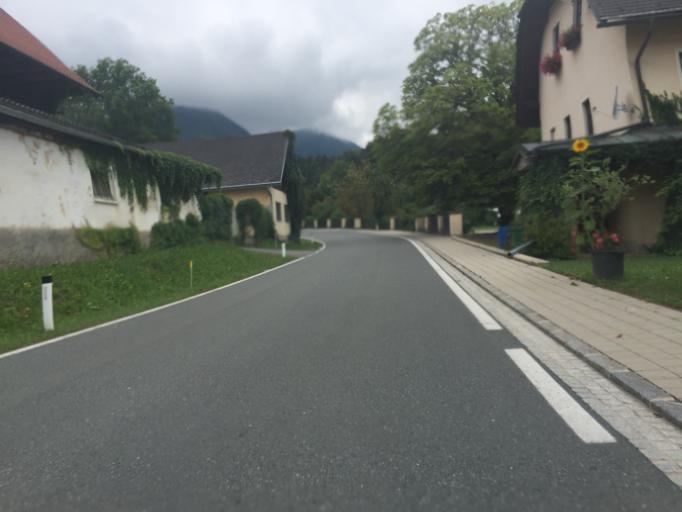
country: AT
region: Carinthia
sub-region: Politischer Bezirk Volkermarkt
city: Feistritz ob Bleiburg
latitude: 46.5553
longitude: 14.7669
